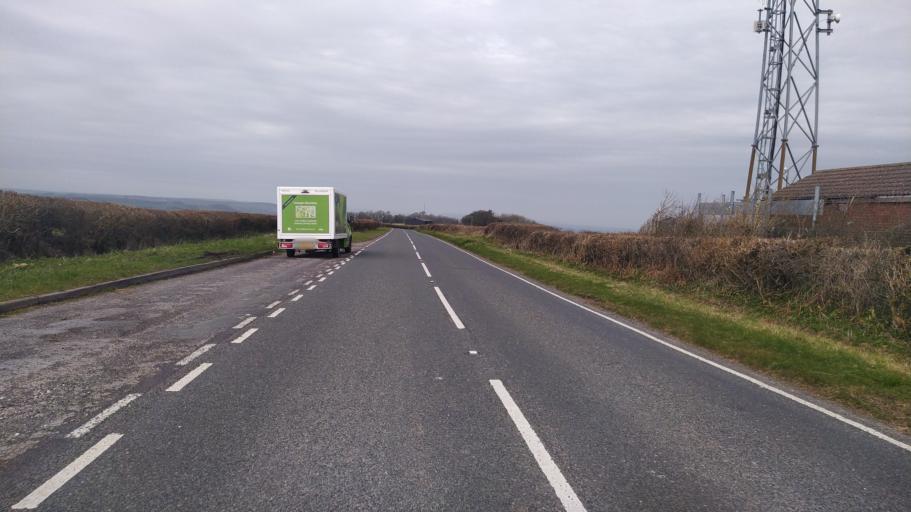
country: GB
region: England
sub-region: Dorset
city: Beaminster
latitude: 50.8424
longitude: -2.7115
